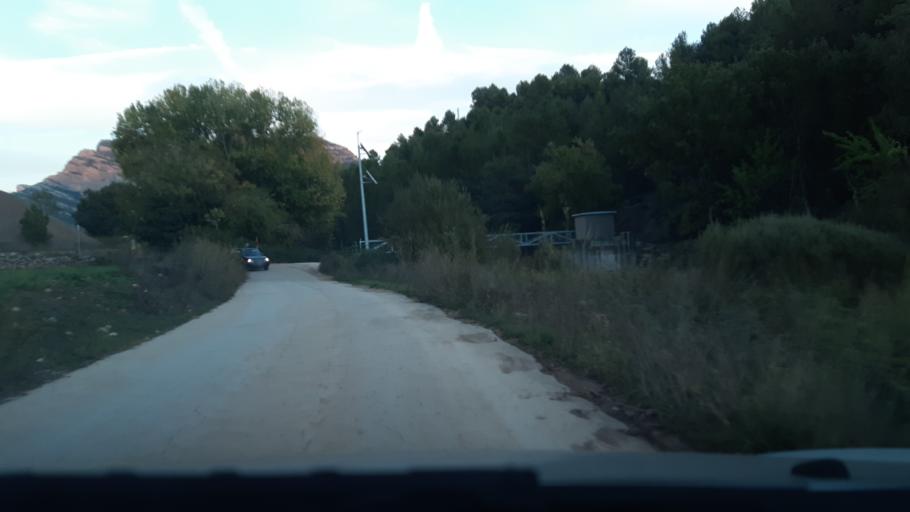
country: ES
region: Aragon
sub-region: Provincia de Teruel
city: Valderrobres
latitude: 40.8403
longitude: 0.1968
